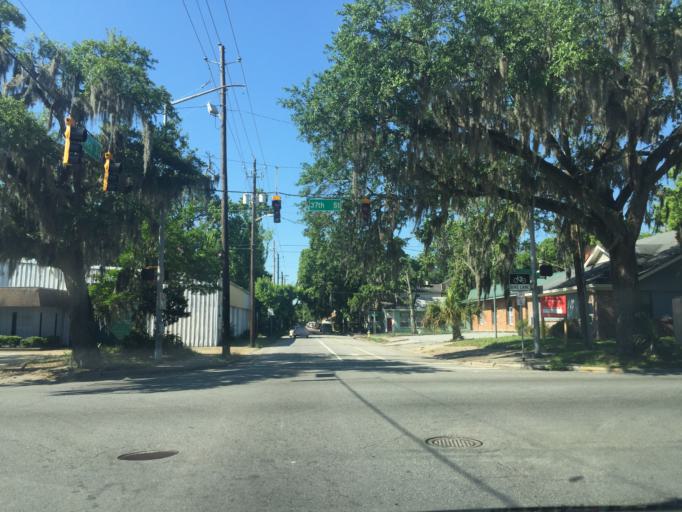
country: US
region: Georgia
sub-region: Chatham County
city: Savannah
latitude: 32.0560
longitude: -81.0946
